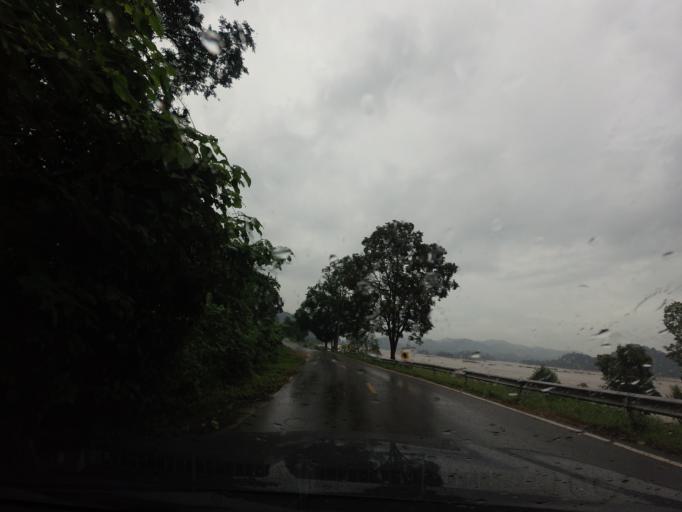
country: TH
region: Nong Khai
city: Sangkhom
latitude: 18.2030
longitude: 102.1592
